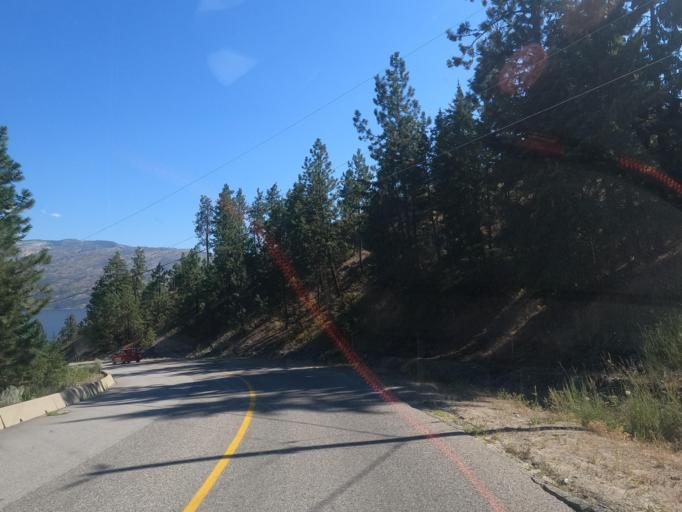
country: CA
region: British Columbia
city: Peachland
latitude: 49.7914
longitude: -119.7106
